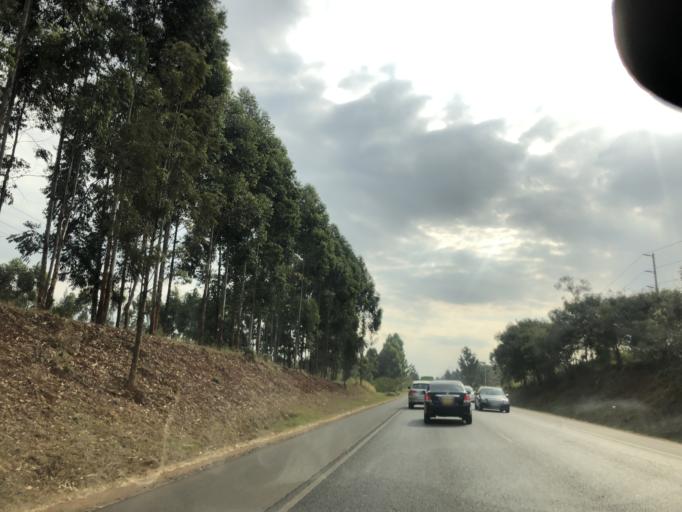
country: KE
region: Kiambu
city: Kiambu
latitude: -1.2152
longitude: 36.8581
